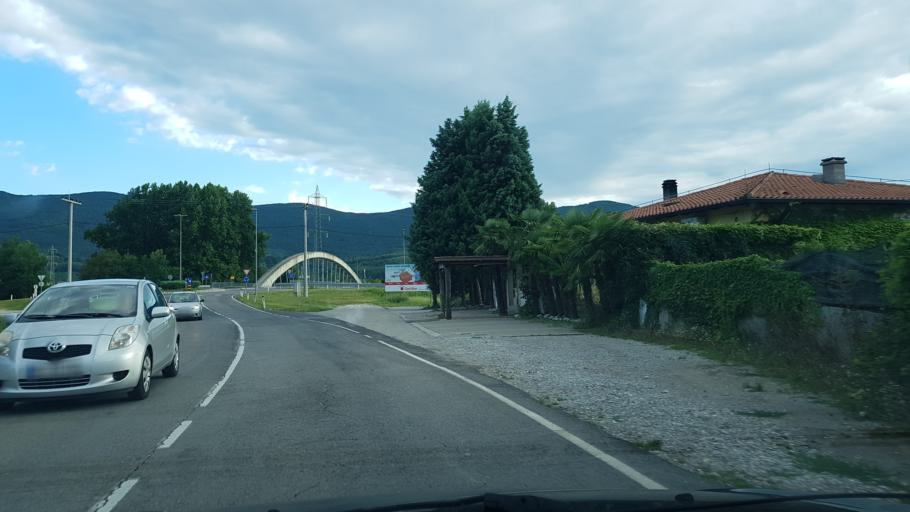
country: SI
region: Rence-Vogrsko
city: Rence
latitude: 45.8933
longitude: 13.6667
